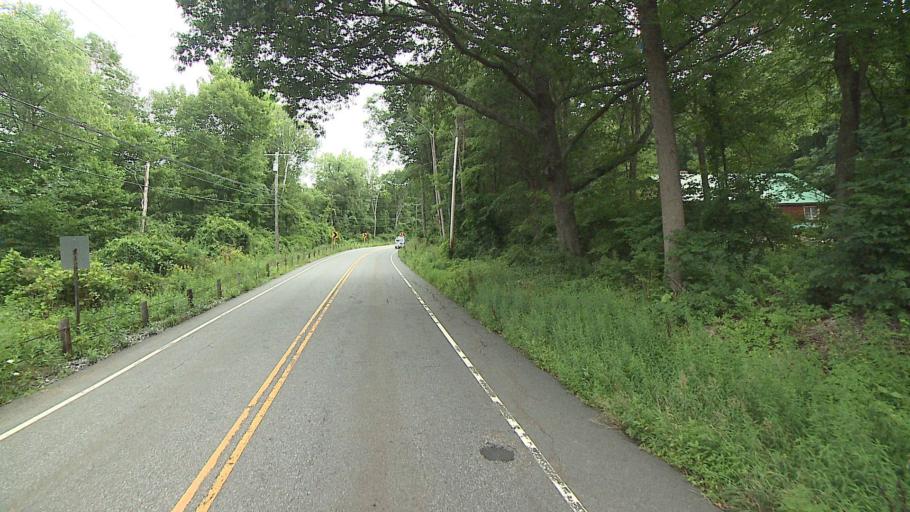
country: US
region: Connecticut
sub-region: Litchfield County
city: Kent
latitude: 41.7204
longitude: -73.4545
